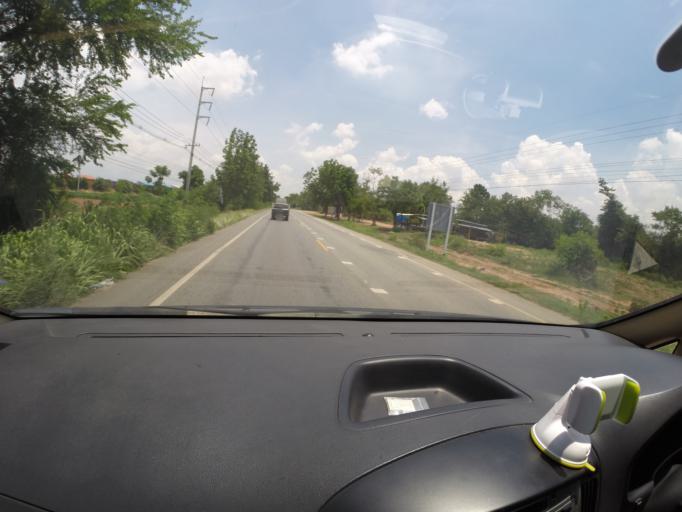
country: TH
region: Nakhon Ratchasima
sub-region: Amphoe Thepharak
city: Thepharak
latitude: 15.1283
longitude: 101.5612
